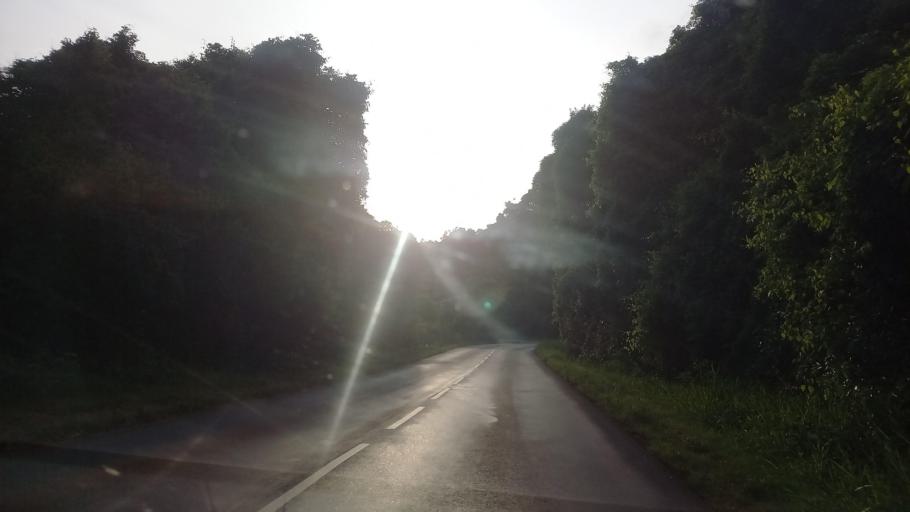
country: YT
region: Tsingoni
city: Tsingoni
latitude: -12.7609
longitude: 45.1113
